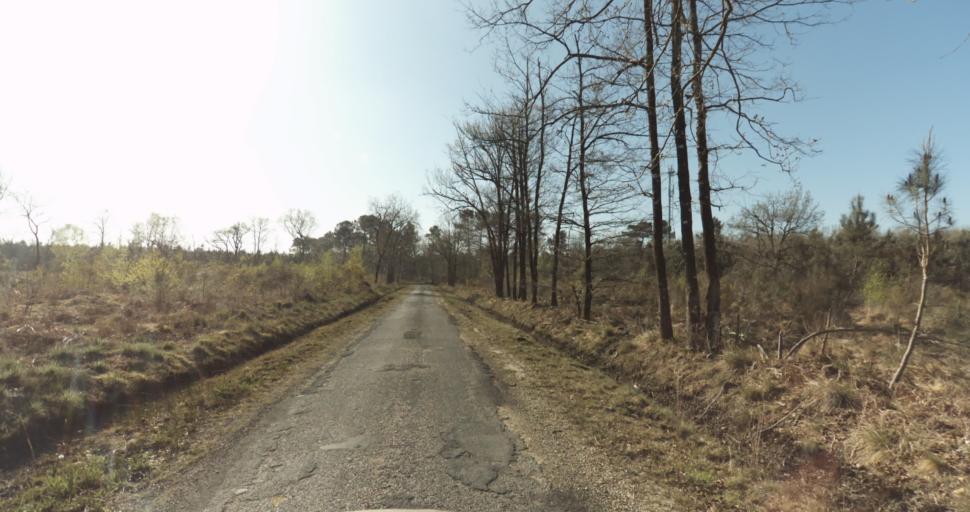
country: FR
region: Aquitaine
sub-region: Departement de la Gironde
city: Martignas-sur-Jalle
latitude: 44.8082
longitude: -0.8496
